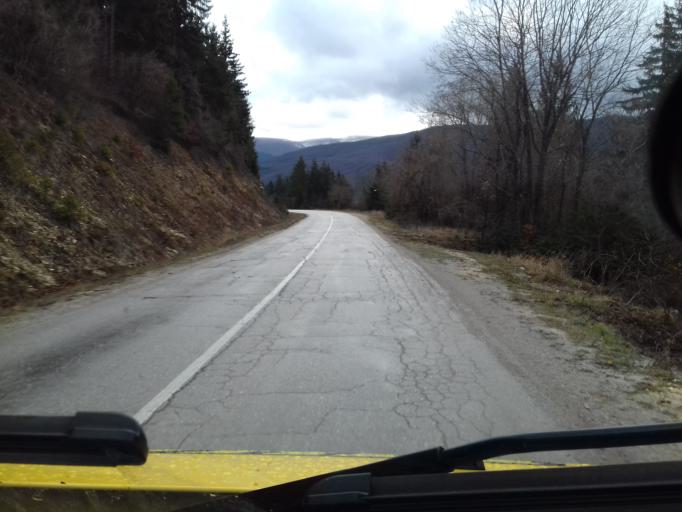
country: BA
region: Federation of Bosnia and Herzegovina
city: Turbe
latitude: 44.2814
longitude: 17.5081
